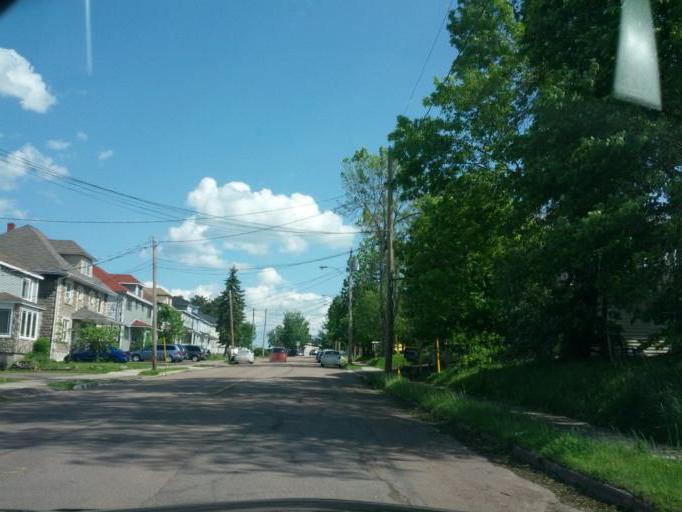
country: CA
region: New Brunswick
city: Moncton
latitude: 46.0953
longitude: -64.7754
